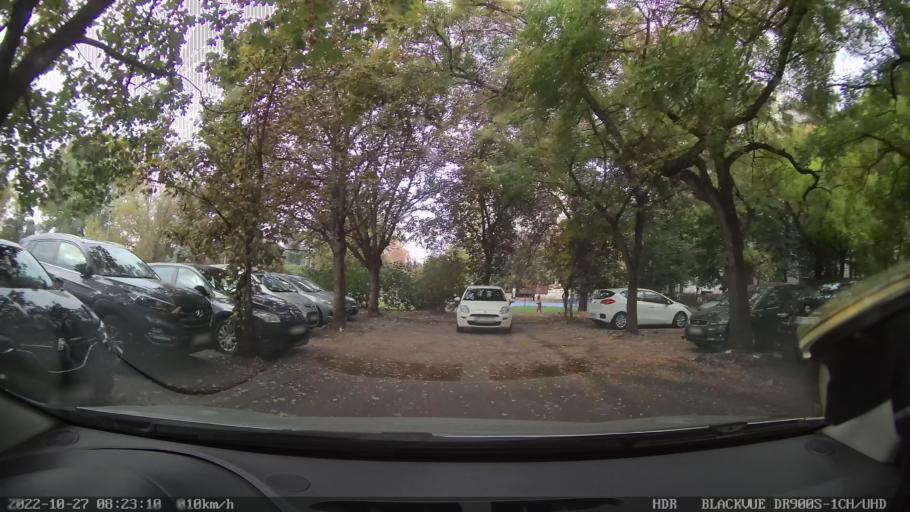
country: RS
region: Central Serbia
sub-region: Belgrade
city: Novi Beograd
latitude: 44.8011
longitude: 20.3977
